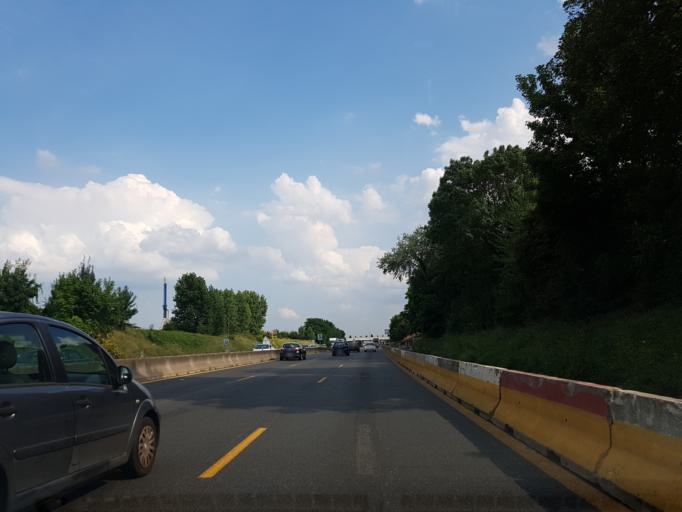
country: FR
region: Ile-de-France
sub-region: Departement de l'Essonne
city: Grigny
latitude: 48.6558
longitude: 2.3785
